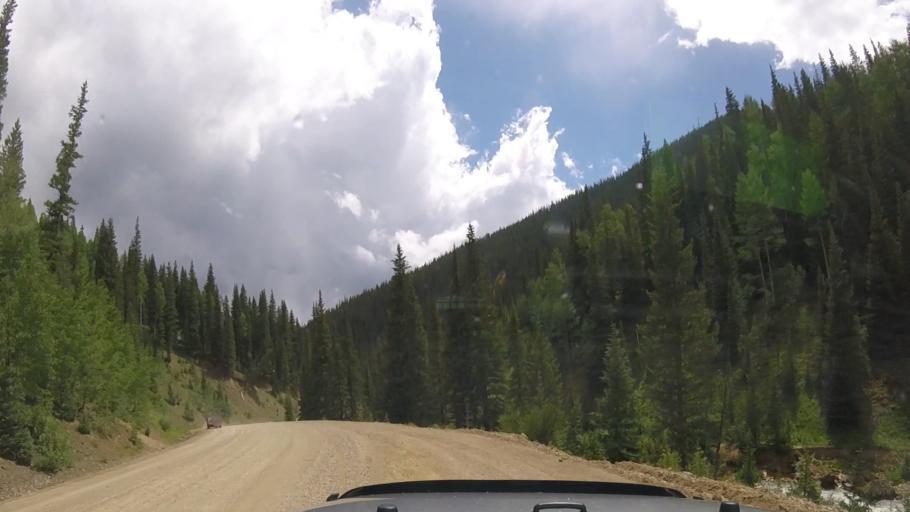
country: US
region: Colorado
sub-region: San Juan County
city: Silverton
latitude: 37.8370
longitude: -107.6779
